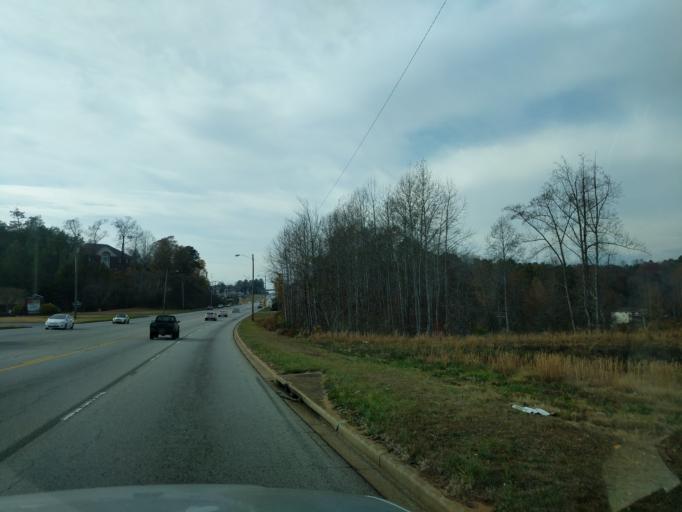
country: US
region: South Carolina
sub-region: Oconee County
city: Seneca
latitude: 34.6976
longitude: -82.9462
